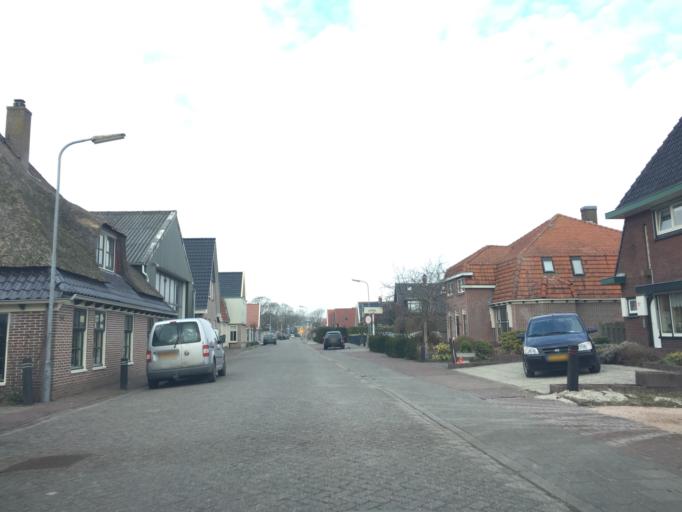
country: NL
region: North Holland
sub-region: Gemeente Schagen
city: Harenkarspel
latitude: 52.7462
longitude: 4.7782
